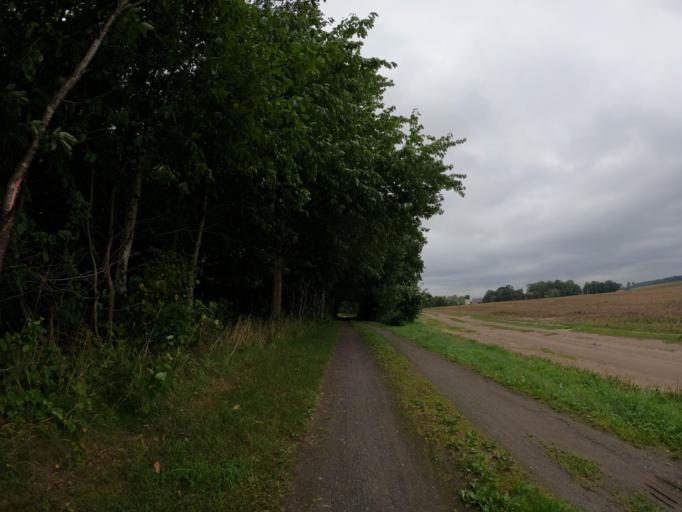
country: DE
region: Mecklenburg-Vorpommern
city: Garz
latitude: 54.3323
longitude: 13.3638
